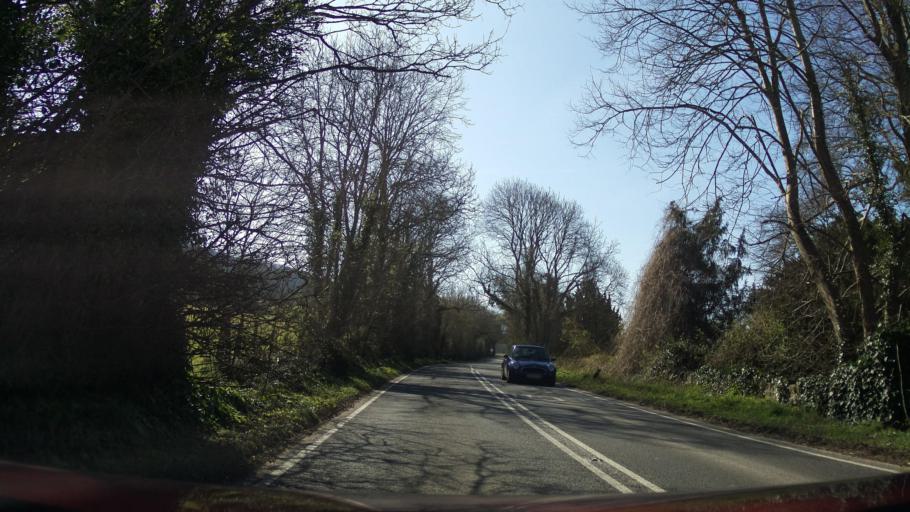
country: GB
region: England
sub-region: Bath and North East Somerset
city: Freshford
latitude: 51.3947
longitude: -2.3050
